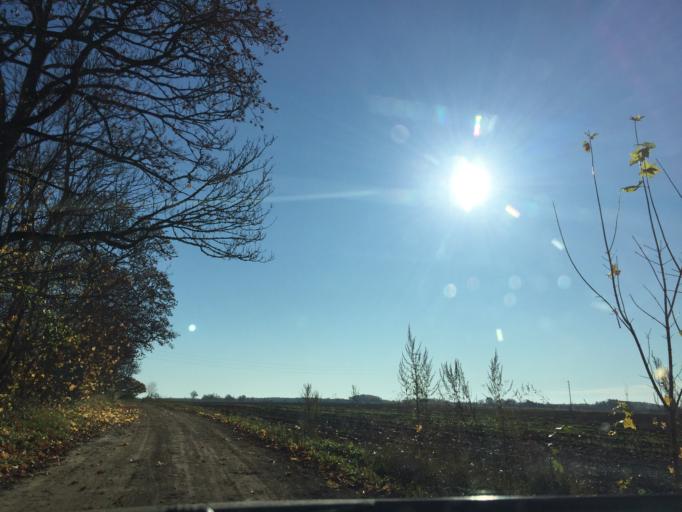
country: LV
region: Skriveri
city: Skriveri
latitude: 56.6835
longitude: 25.1450
